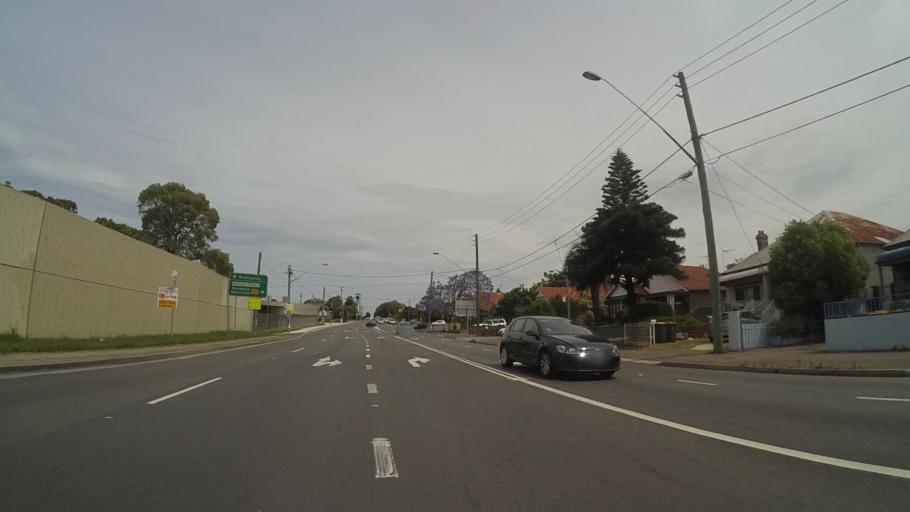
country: AU
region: New South Wales
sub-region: Rockdale
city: Arncliffe
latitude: -33.9387
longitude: 151.1516
